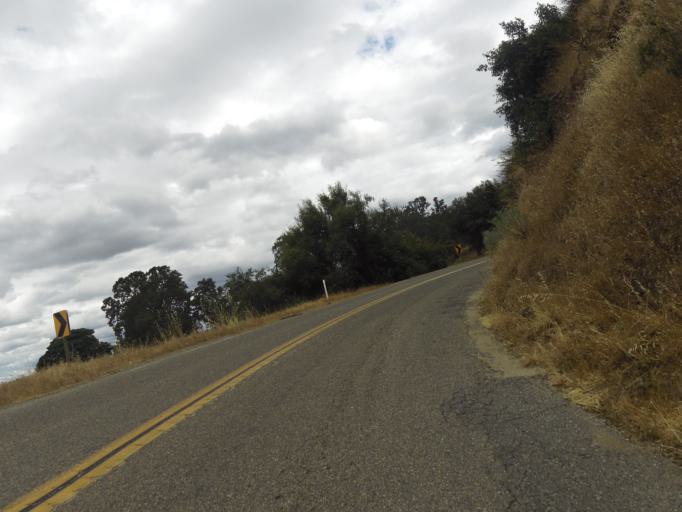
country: US
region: California
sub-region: Madera County
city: Ahwahnee
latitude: 37.3005
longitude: -119.7950
